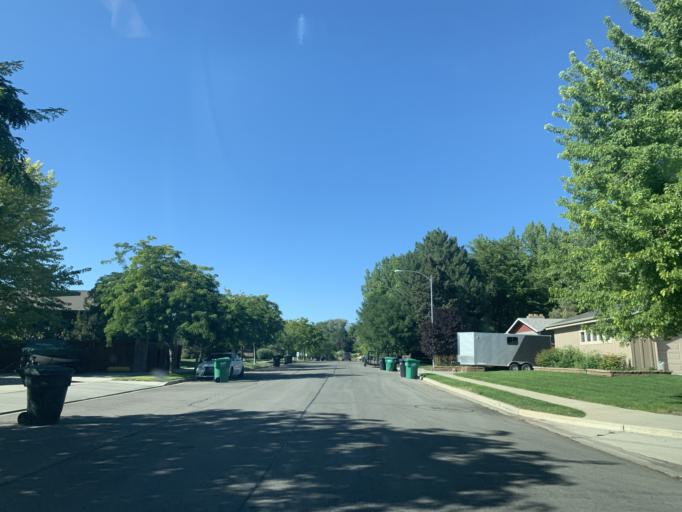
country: US
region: Utah
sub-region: Utah County
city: Provo
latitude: 40.2579
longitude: -111.6853
